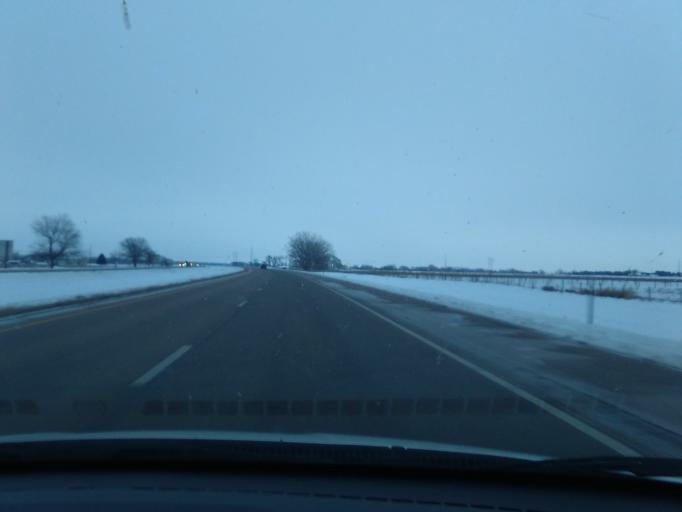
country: US
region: Nebraska
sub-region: Keith County
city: Ogallala
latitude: 41.1153
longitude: -101.7027
